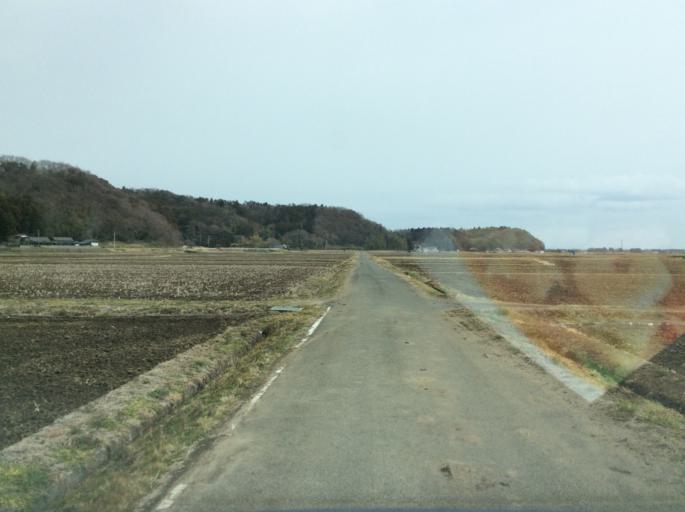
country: JP
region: Fukushima
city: Iwaki
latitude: 37.0927
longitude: 140.9433
